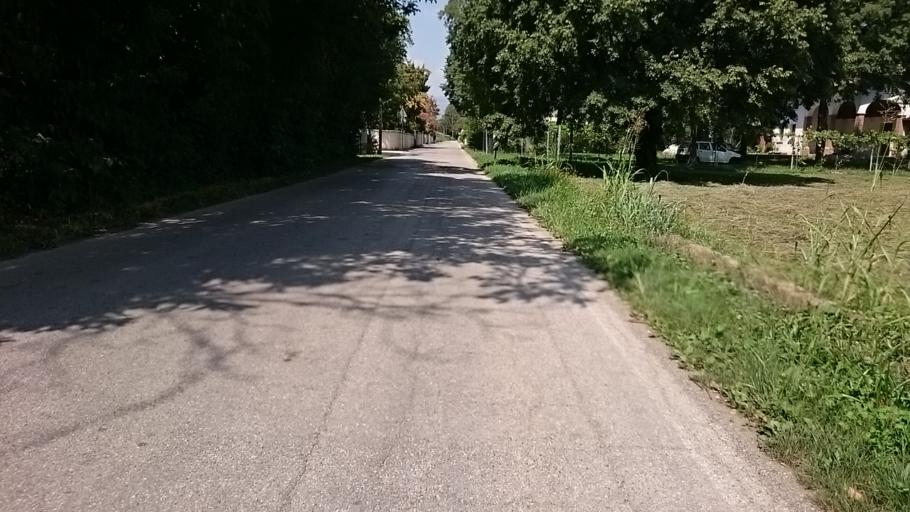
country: IT
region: Veneto
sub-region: Provincia di Vicenza
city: Rosa
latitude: 45.6987
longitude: 11.7423
